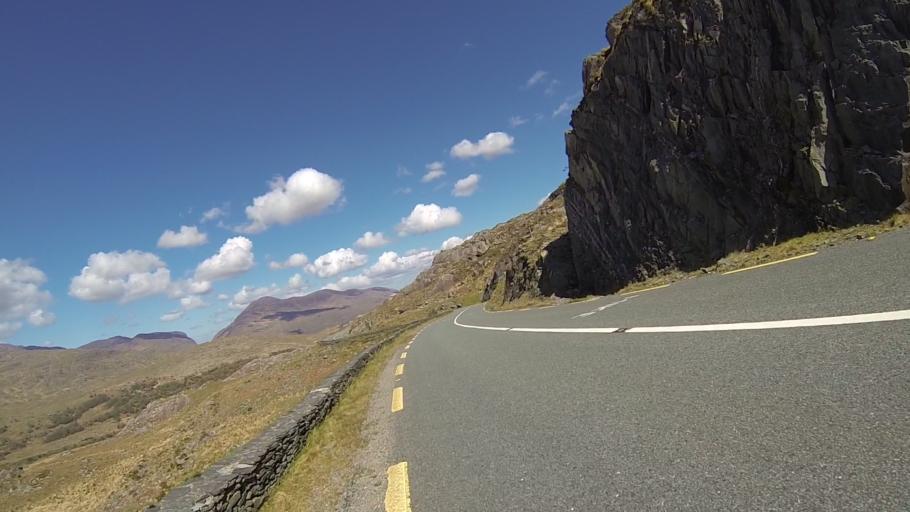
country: IE
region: Munster
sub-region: Ciarrai
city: Kenmare
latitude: 51.9396
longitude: -9.6547
